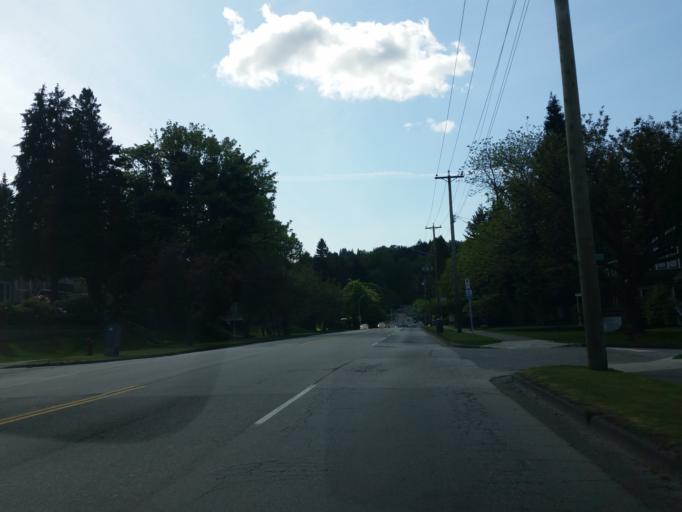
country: CA
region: British Columbia
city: Port Moody
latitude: 49.2767
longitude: -122.8614
